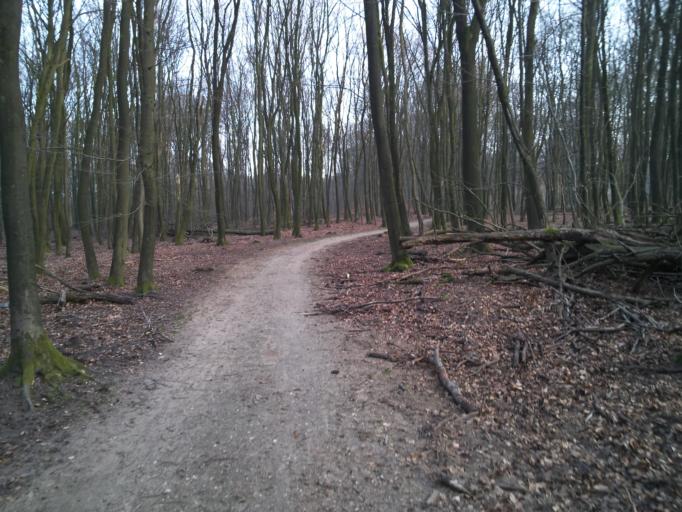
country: NL
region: Gelderland
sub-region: Gemeente Epe
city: Vaassen
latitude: 52.3158
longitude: 5.8770
